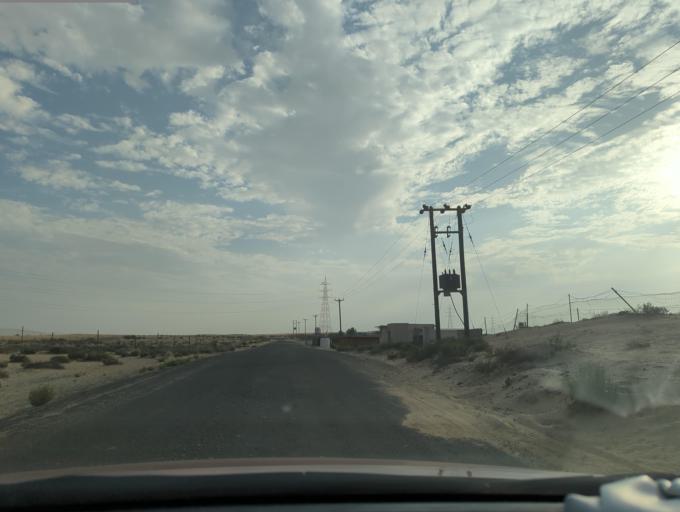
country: AE
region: Dubai
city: Dubai
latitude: 24.7162
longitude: 54.8724
